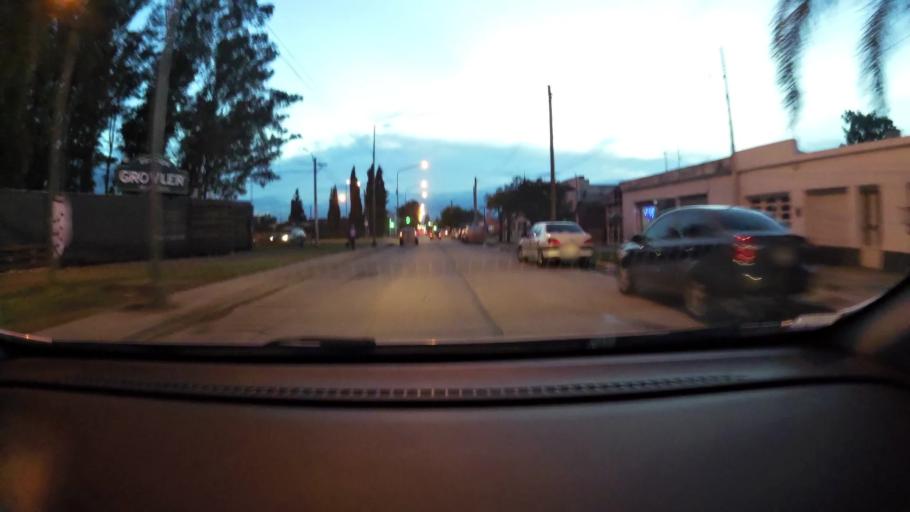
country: AR
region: Buenos Aires
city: San Nicolas de los Arroyos
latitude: -33.3436
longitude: -60.2296
